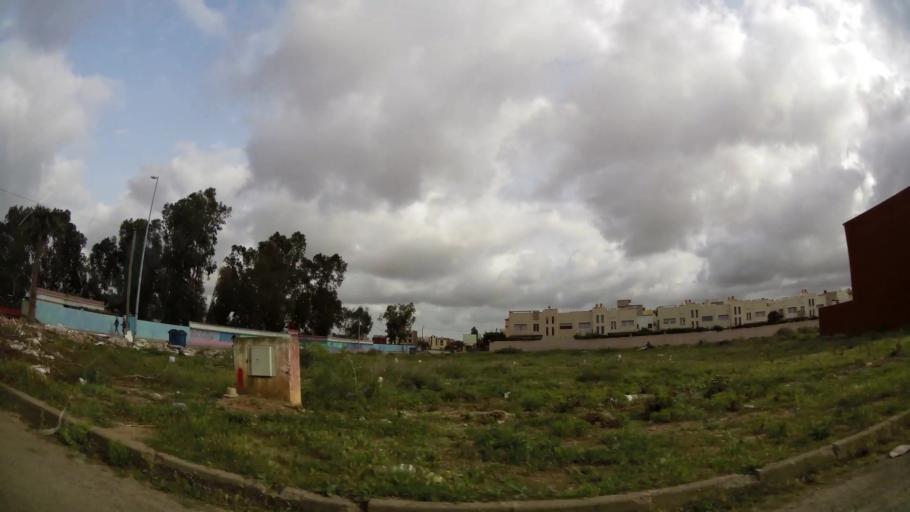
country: MA
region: Oriental
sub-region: Nador
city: Nador
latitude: 35.1613
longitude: -2.9165
